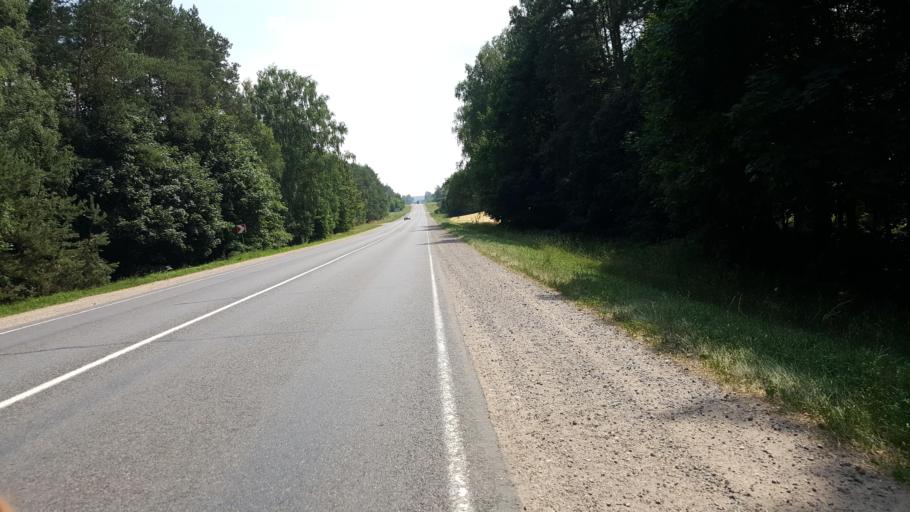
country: BY
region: Brest
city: Kamyanyets
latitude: 52.3428
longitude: 23.7803
